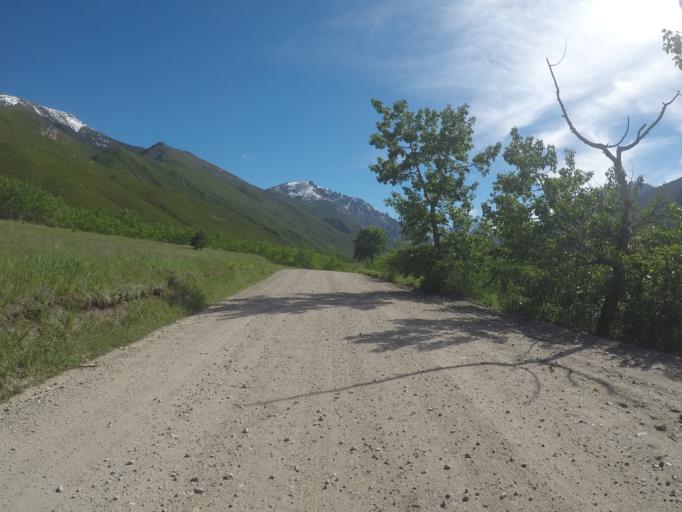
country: US
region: Montana
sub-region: Stillwater County
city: Absarokee
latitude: 45.2593
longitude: -109.5656
